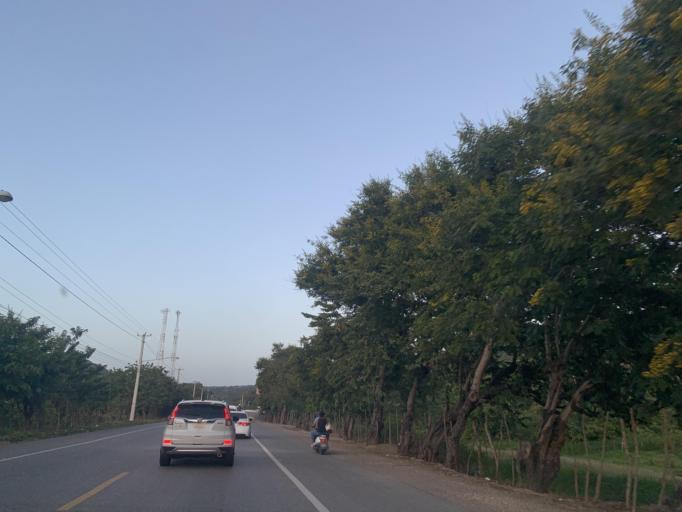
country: DO
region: Puerto Plata
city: Imbert
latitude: 19.7957
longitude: -70.7960
